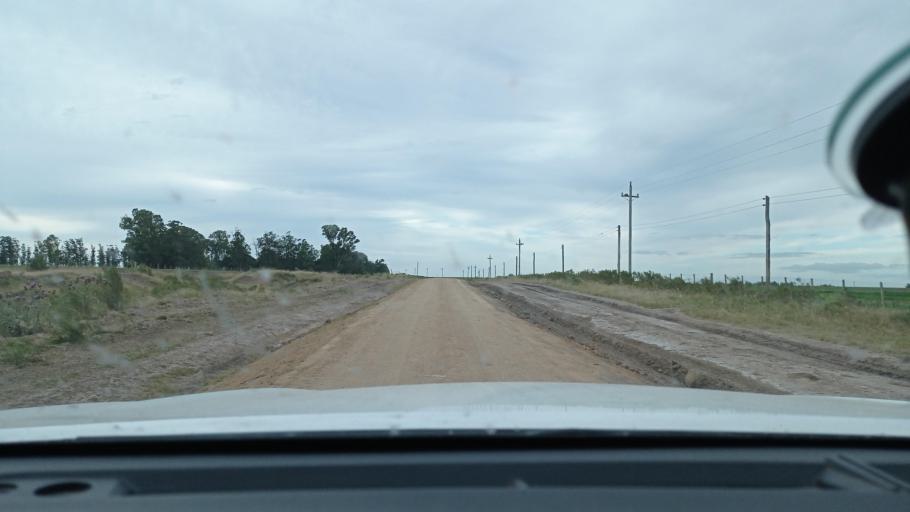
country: UY
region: Florida
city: Casupa
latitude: -34.1135
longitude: -55.7670
